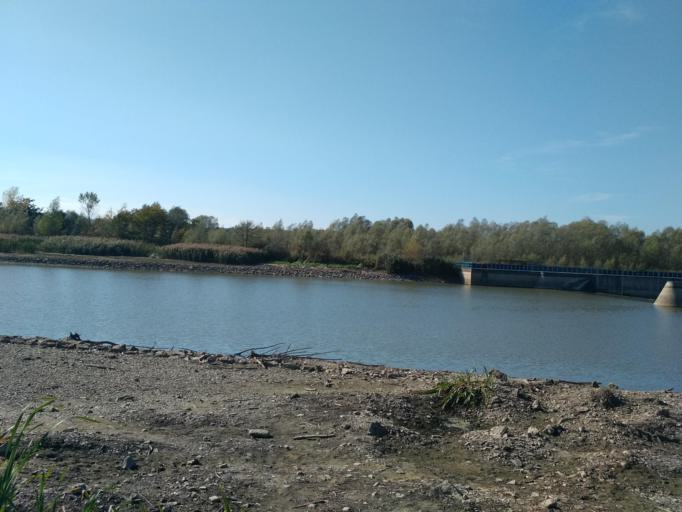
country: PL
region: Subcarpathian Voivodeship
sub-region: Powiat debicki
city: Pilzno
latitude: 49.9742
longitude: 21.3169
